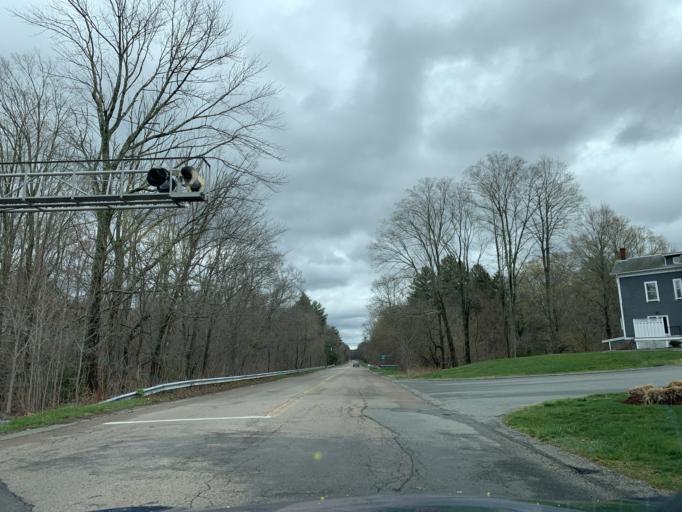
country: US
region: Massachusetts
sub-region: Bristol County
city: Norton
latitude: 41.9456
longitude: -71.2209
